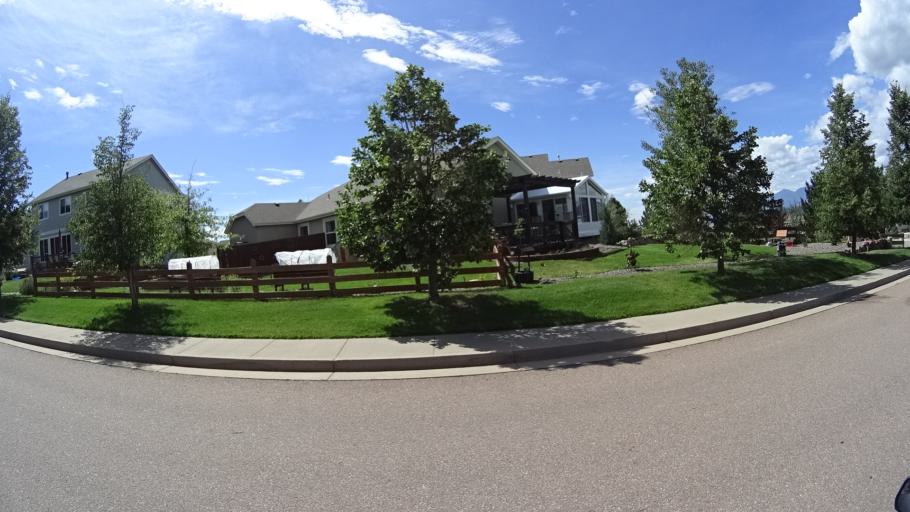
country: US
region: Colorado
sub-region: El Paso County
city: Gleneagle
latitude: 39.0283
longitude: -104.8219
